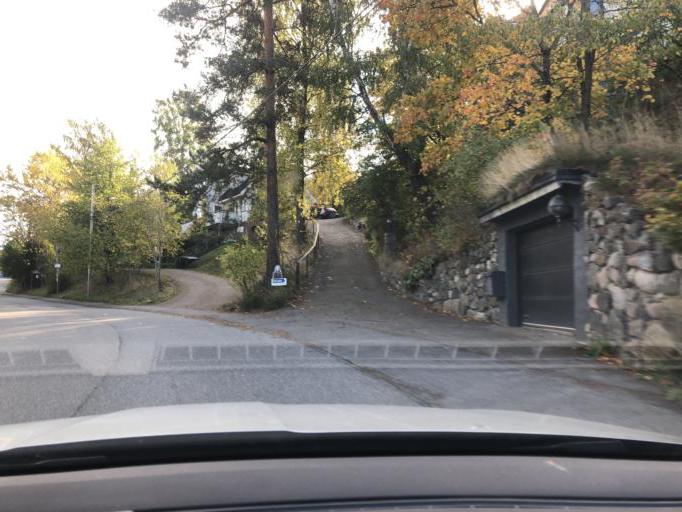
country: SE
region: Stockholm
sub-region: Nacka Kommun
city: Nacka
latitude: 59.2987
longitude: 18.1538
